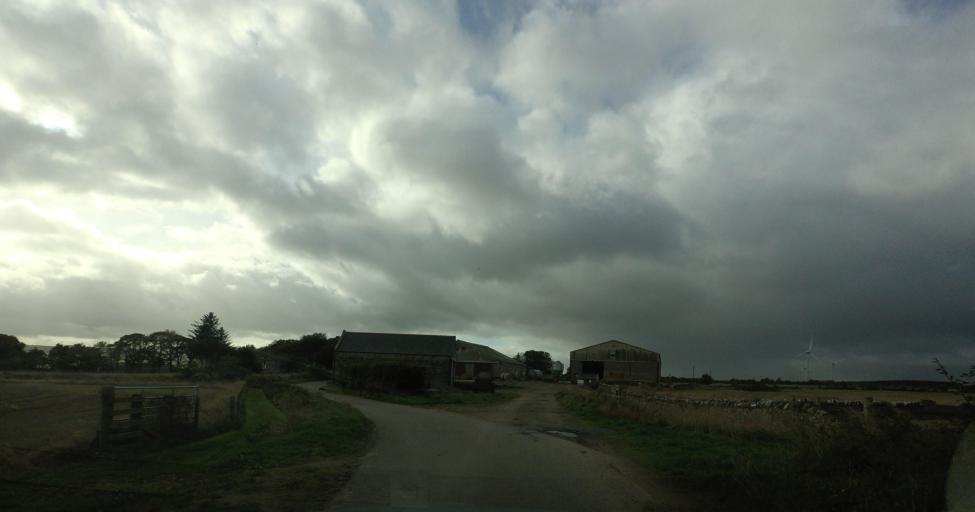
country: GB
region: Scotland
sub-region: Aberdeenshire
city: Whitehills
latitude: 57.6654
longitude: -2.5992
